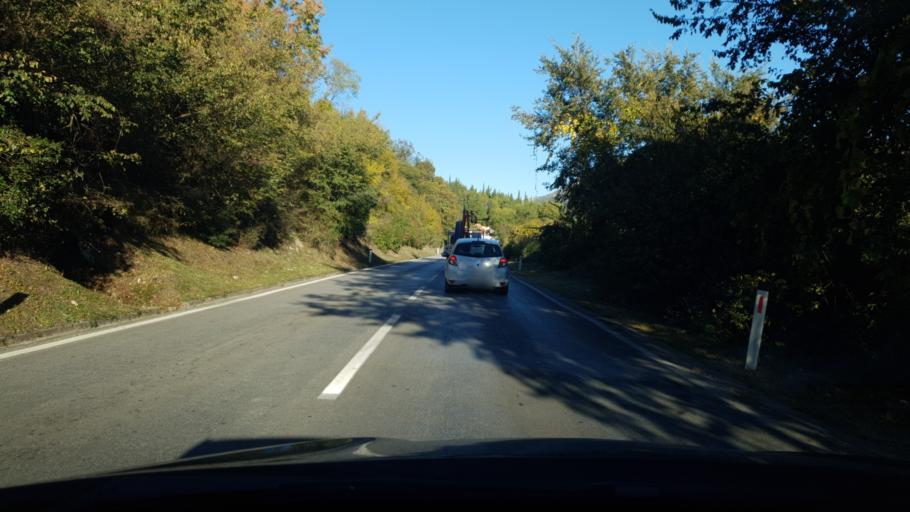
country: ME
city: Igalo
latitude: 42.4604
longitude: 18.4883
